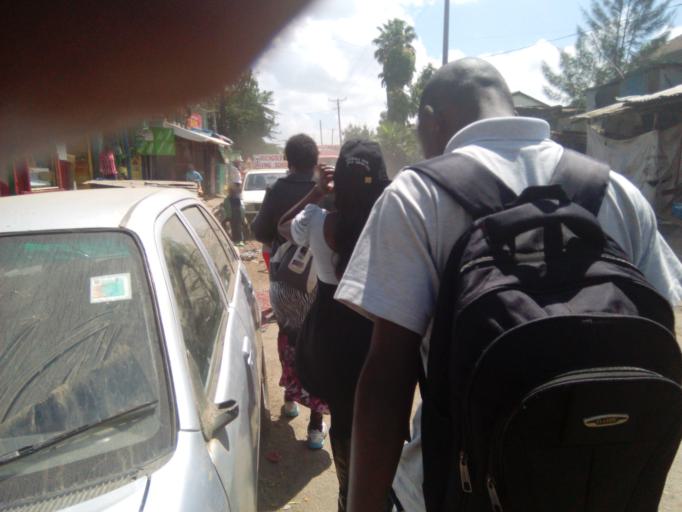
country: KE
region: Nairobi Area
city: Pumwani
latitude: -1.3125
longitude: 36.8437
